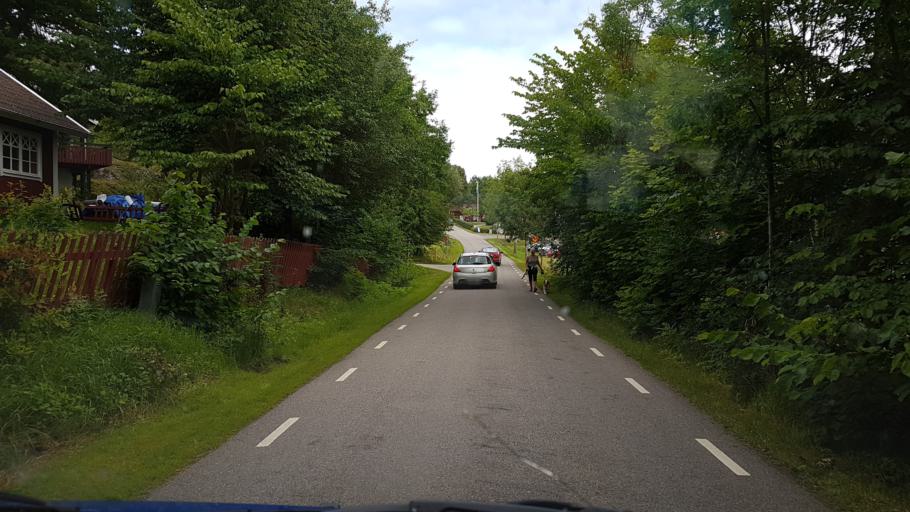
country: SE
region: OEstergoetland
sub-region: Valdemarsviks Kommun
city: Gusum
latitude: 58.4450
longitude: 16.5973
